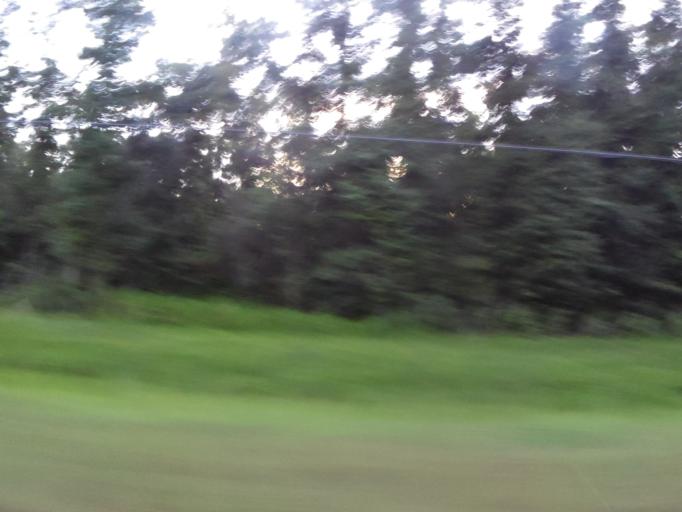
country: US
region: Georgia
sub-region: Camden County
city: Woodbine
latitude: 30.9455
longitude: -81.7192
